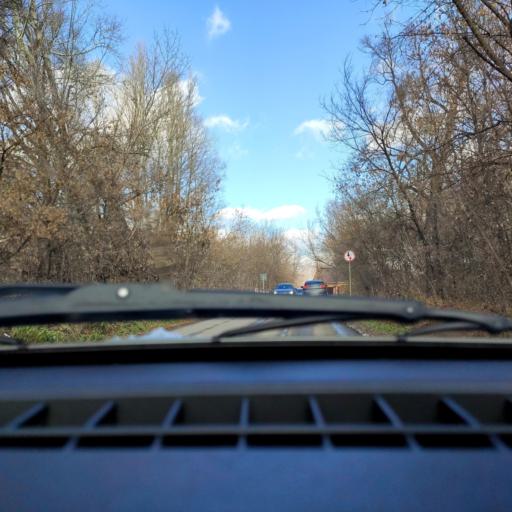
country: RU
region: Bashkortostan
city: Ufa
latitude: 54.8039
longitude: 56.1510
